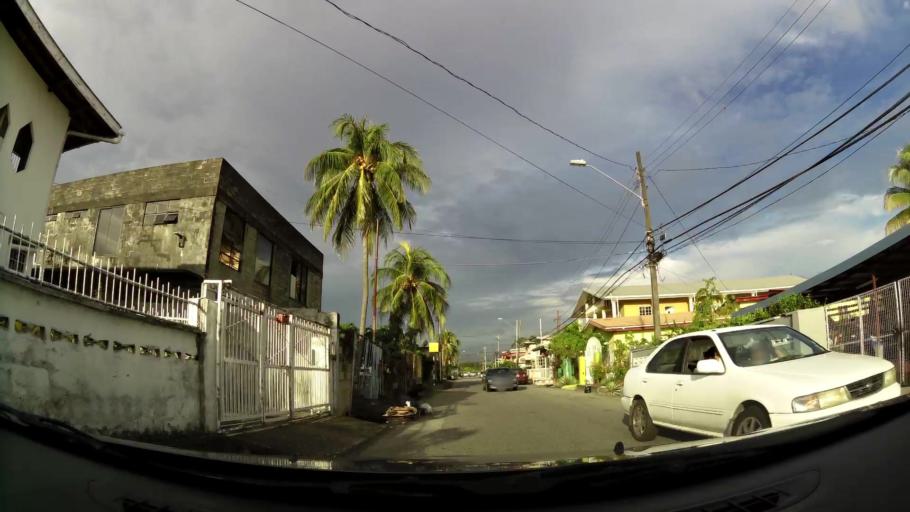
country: TT
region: Tunapuna/Piarco
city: Tunapuna
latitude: 10.6427
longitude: -61.4081
